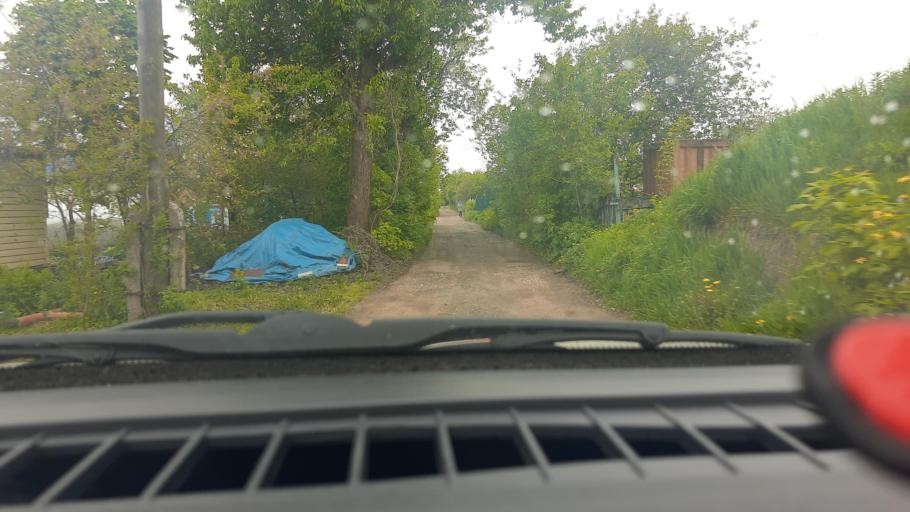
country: RU
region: Nizjnij Novgorod
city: Burevestnik
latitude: 56.2159
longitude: 43.8512
